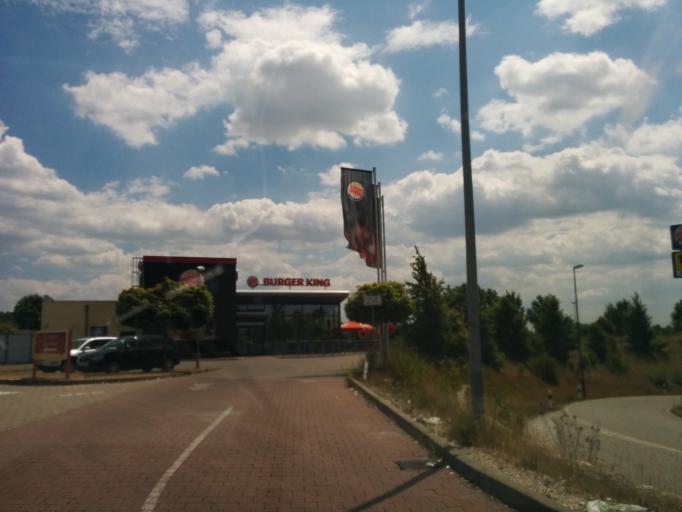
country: DE
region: Bavaria
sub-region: Swabia
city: Gersthofen
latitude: 48.4366
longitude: 10.8689
